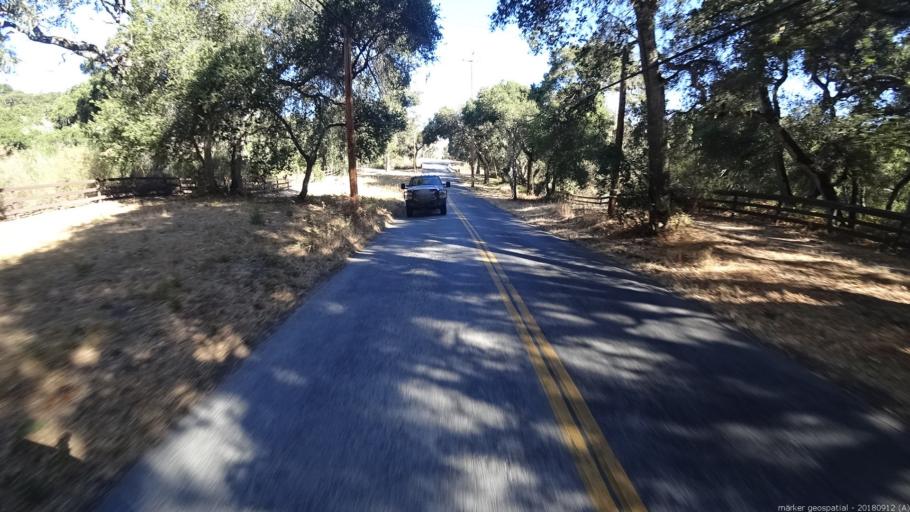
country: US
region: California
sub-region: Monterey County
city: Carmel Valley Village
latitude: 36.5551
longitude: -121.7321
